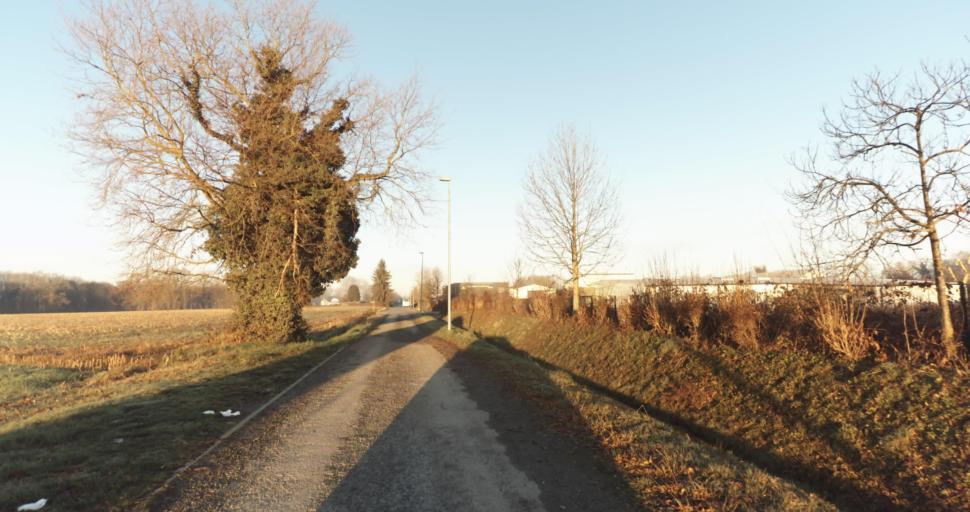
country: FR
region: Aquitaine
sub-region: Departement des Pyrenees-Atlantiques
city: Buros
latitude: 43.3215
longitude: -0.2907
